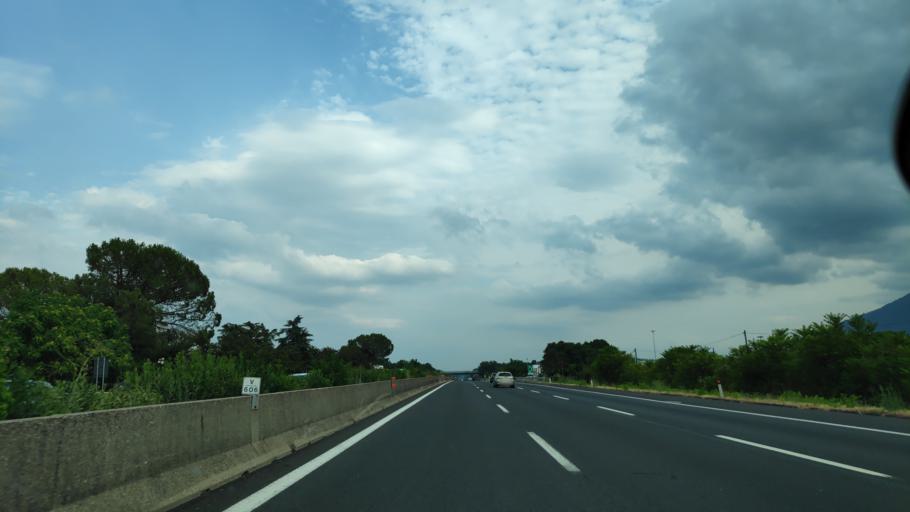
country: IT
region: Latium
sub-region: Provincia di Frosinone
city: Anagni
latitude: 41.7111
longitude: 13.1381
